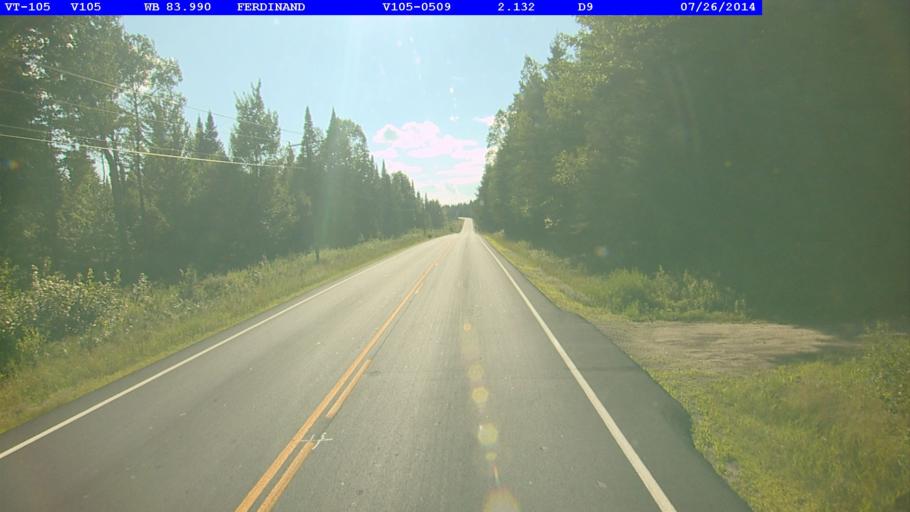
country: US
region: New Hampshire
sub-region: Coos County
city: Stratford
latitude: 44.7800
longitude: -71.7626
